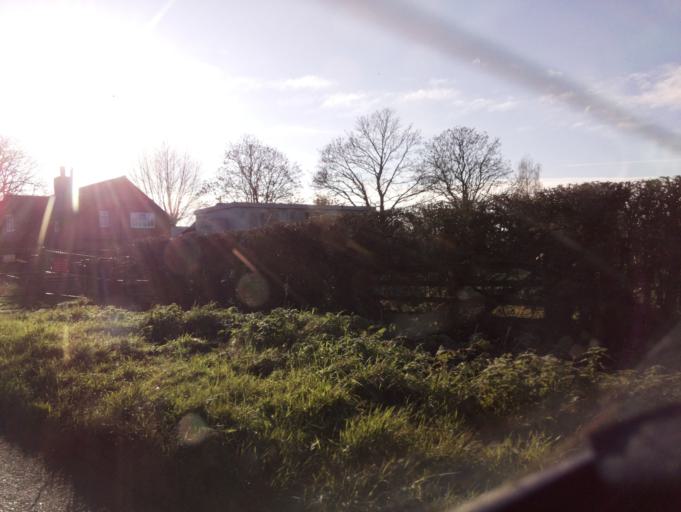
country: GB
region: England
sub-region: Derbyshire
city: Etwall
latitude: 52.8629
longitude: -1.6019
